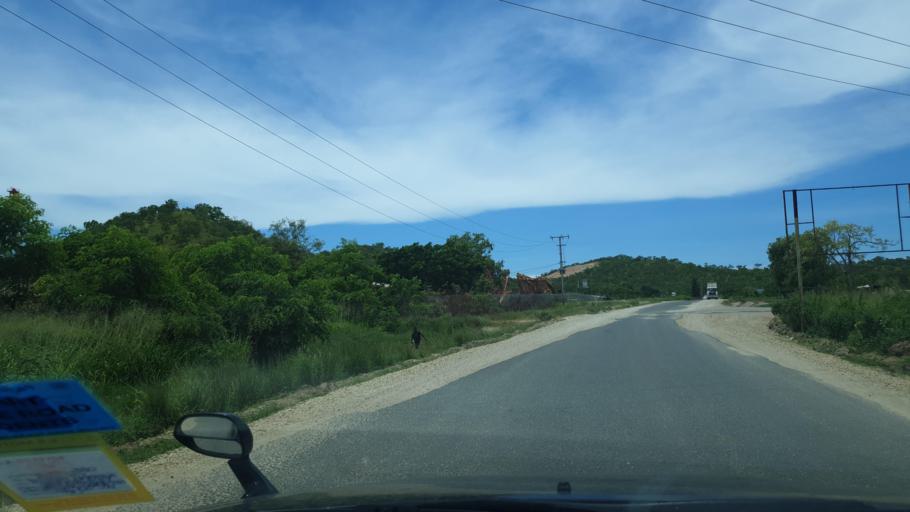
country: PG
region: National Capital
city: Port Moresby
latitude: -9.4280
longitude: 147.0752
